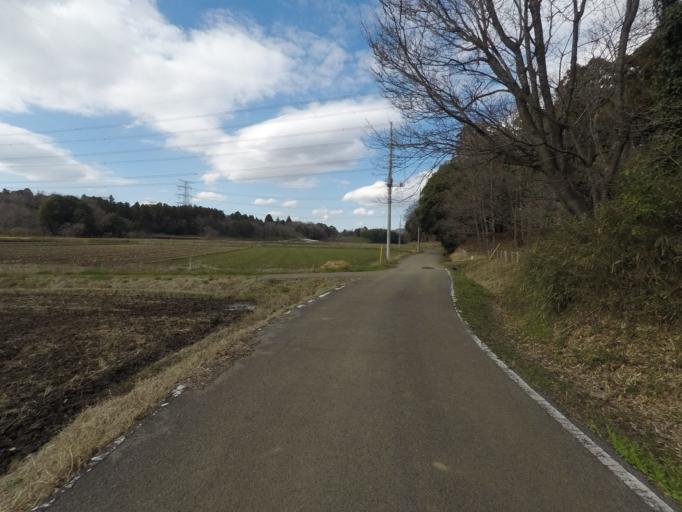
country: JP
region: Ibaraki
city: Ushiku
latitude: 36.0008
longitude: 140.1120
